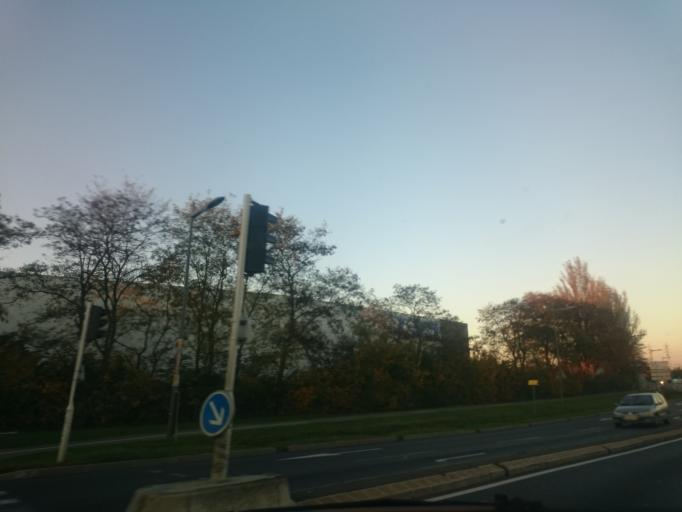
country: FR
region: Ile-de-France
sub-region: Departement de l'Essonne
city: Villabe
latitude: 48.6013
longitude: 2.4413
